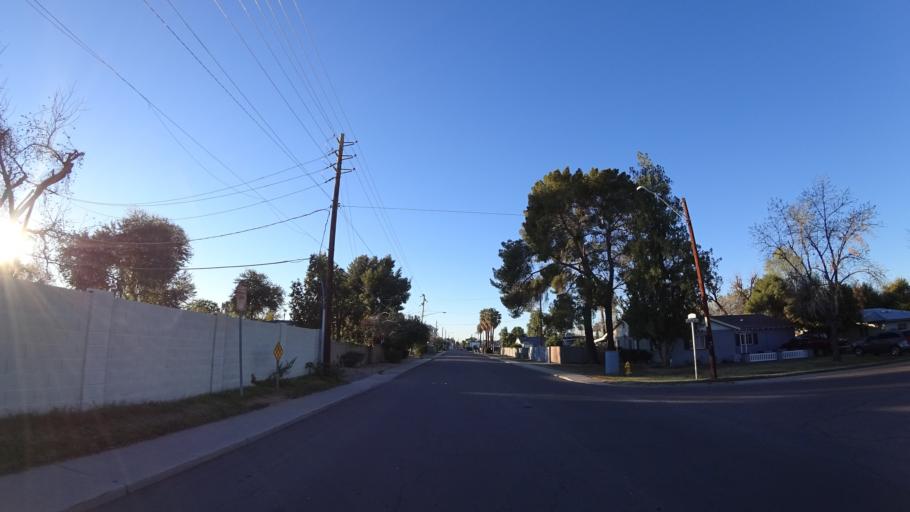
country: US
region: Arizona
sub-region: Maricopa County
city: Paradise Valley
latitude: 33.4832
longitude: -111.9912
